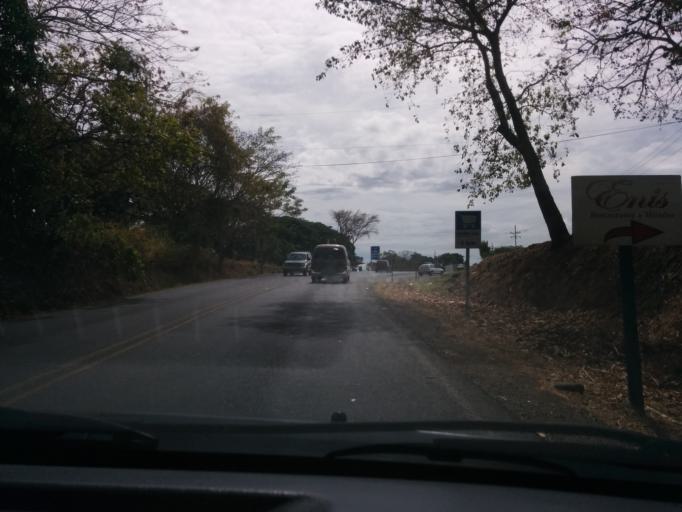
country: CR
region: Puntarenas
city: Esparza
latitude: 9.9977
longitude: -84.6744
